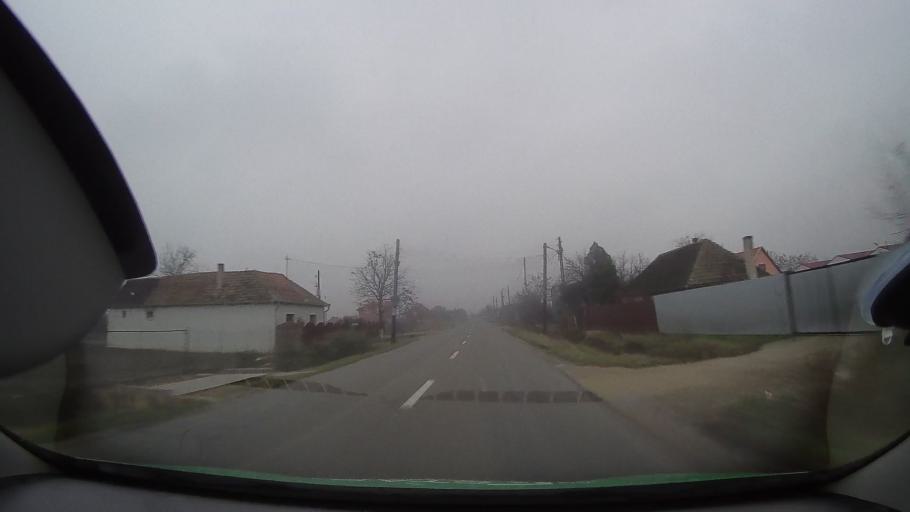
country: RO
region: Bihor
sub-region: Comuna Tulca
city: Tulca
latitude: 46.7942
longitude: 21.7416
